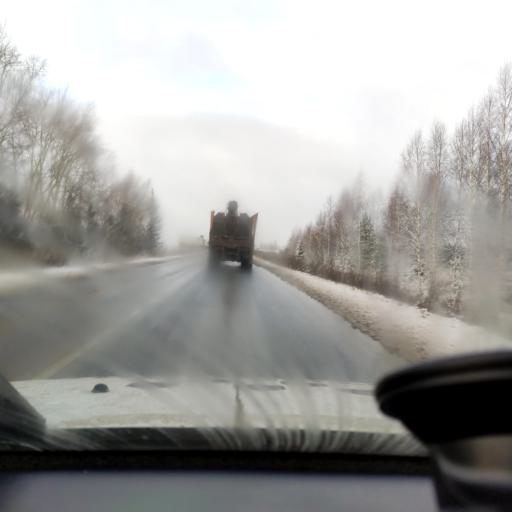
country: RU
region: Perm
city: Nytva
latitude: 57.9433
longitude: 55.3665
